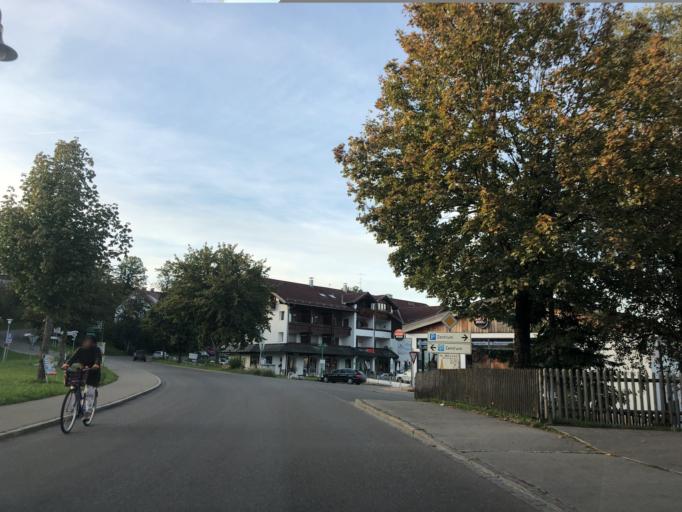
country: DE
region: Bavaria
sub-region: Swabia
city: Pfronten
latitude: 47.5848
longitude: 10.5595
